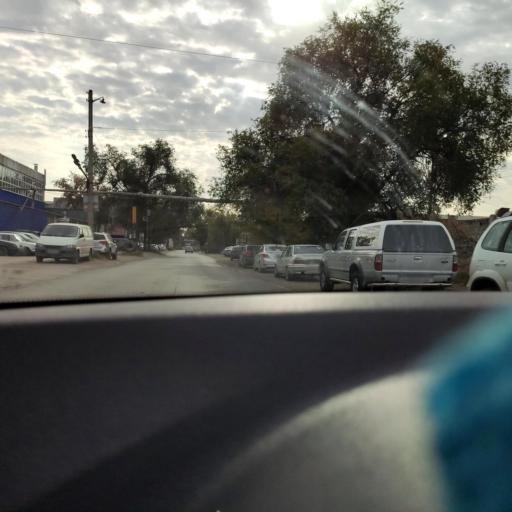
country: RU
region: Samara
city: Samara
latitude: 53.1980
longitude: 50.2578
